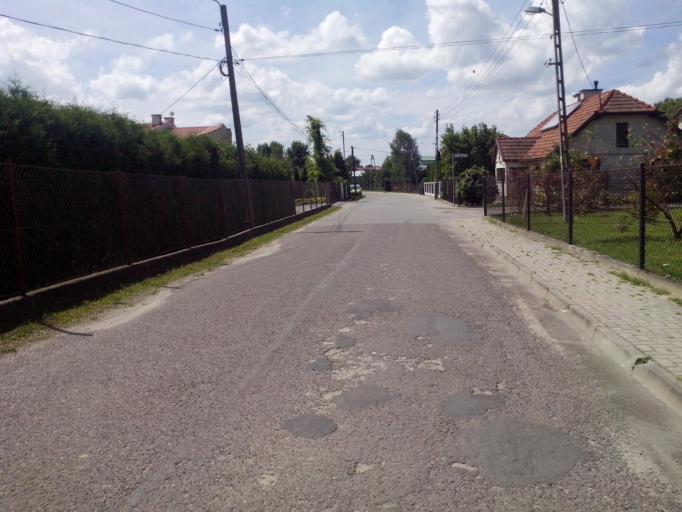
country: PL
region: Subcarpathian Voivodeship
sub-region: Powiat strzyzowski
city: Strzyzow
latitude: 49.8706
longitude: 21.8046
